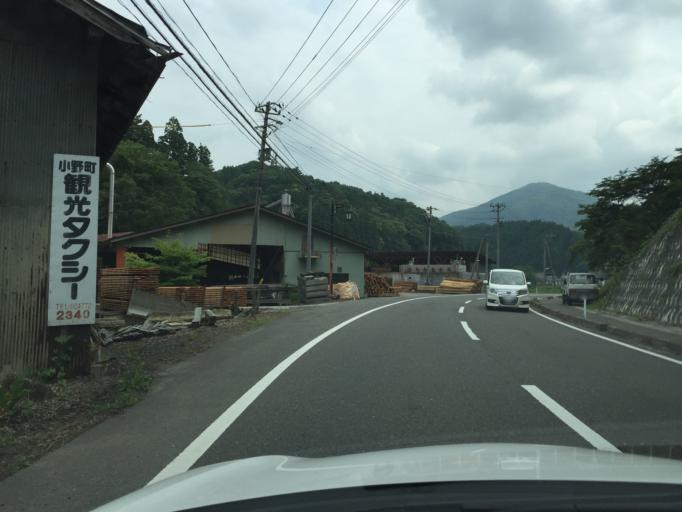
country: JP
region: Fukushima
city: Miharu
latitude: 37.2971
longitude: 140.5405
